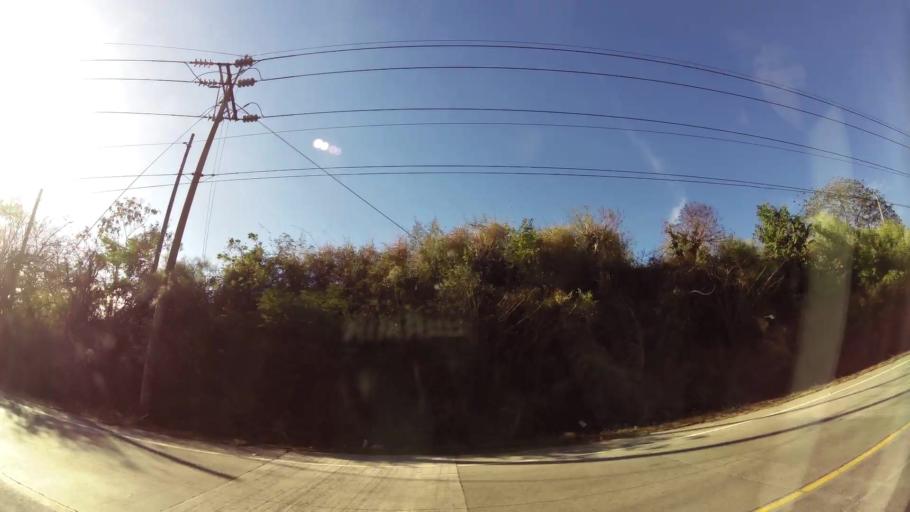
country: SV
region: Santa Ana
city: Metapan
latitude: 14.2536
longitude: -89.4616
